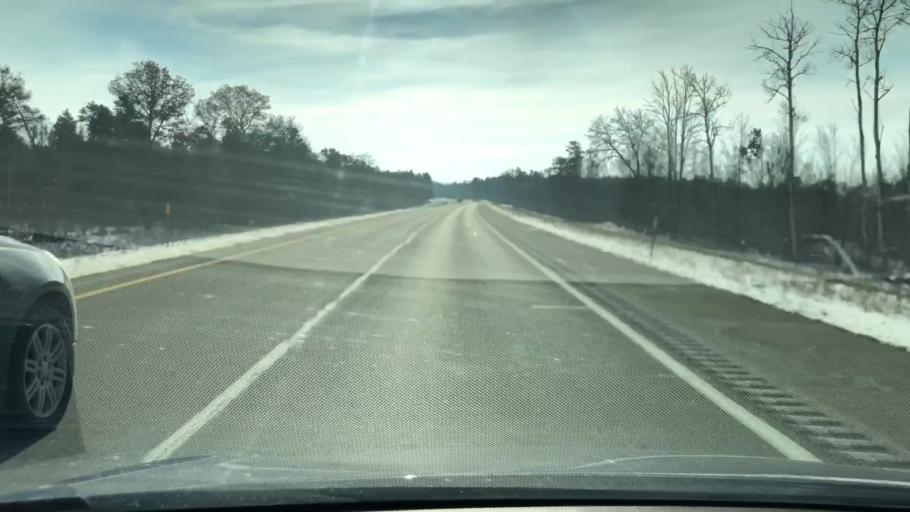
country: US
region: Michigan
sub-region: Crawford County
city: Grayling
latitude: 44.5662
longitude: -84.7083
